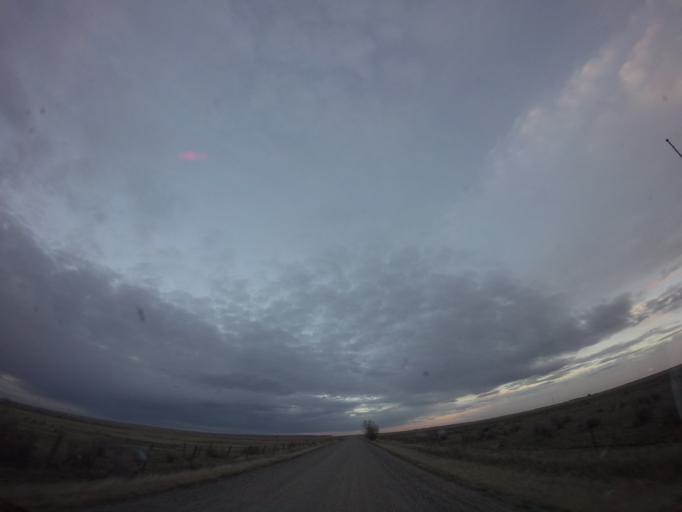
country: US
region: Montana
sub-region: Yellowstone County
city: Laurel
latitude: 45.9439
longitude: -108.7687
